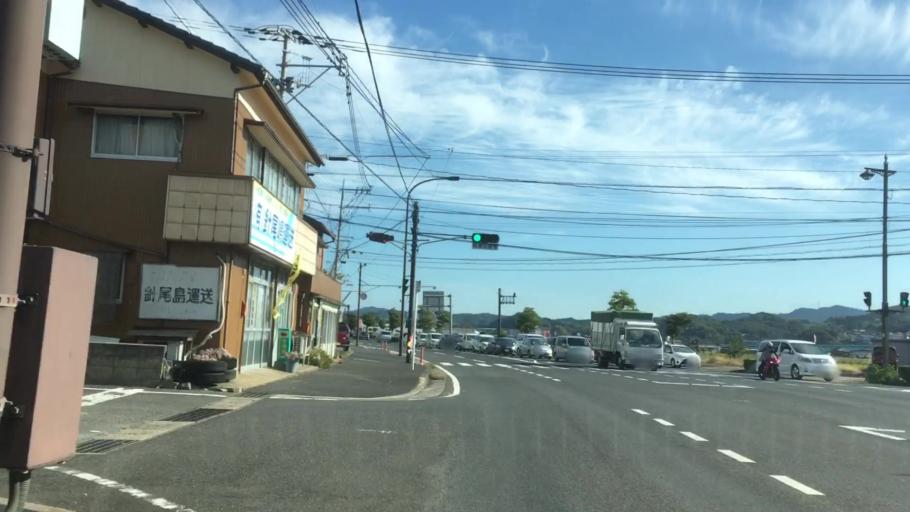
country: JP
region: Nagasaki
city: Sasebo
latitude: 33.1081
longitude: 129.7838
